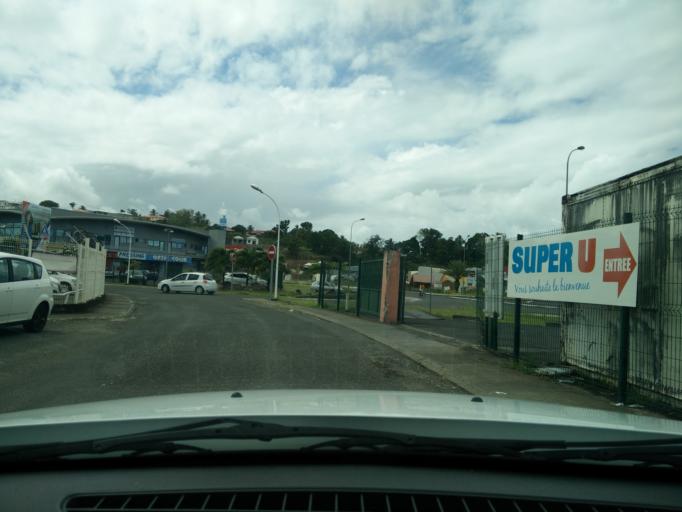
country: GP
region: Guadeloupe
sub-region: Guadeloupe
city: Petit-Bourg
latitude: 16.2019
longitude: -61.6070
